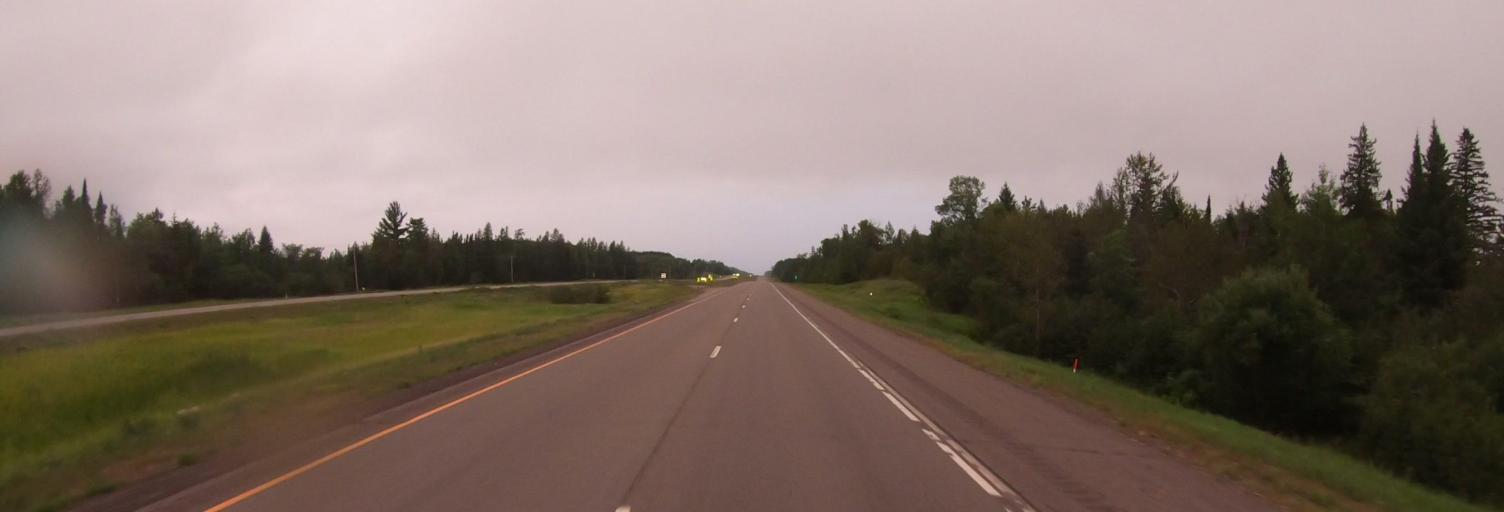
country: US
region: Minnesota
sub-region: Carlton County
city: Cloquet
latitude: 46.9799
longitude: -92.4707
